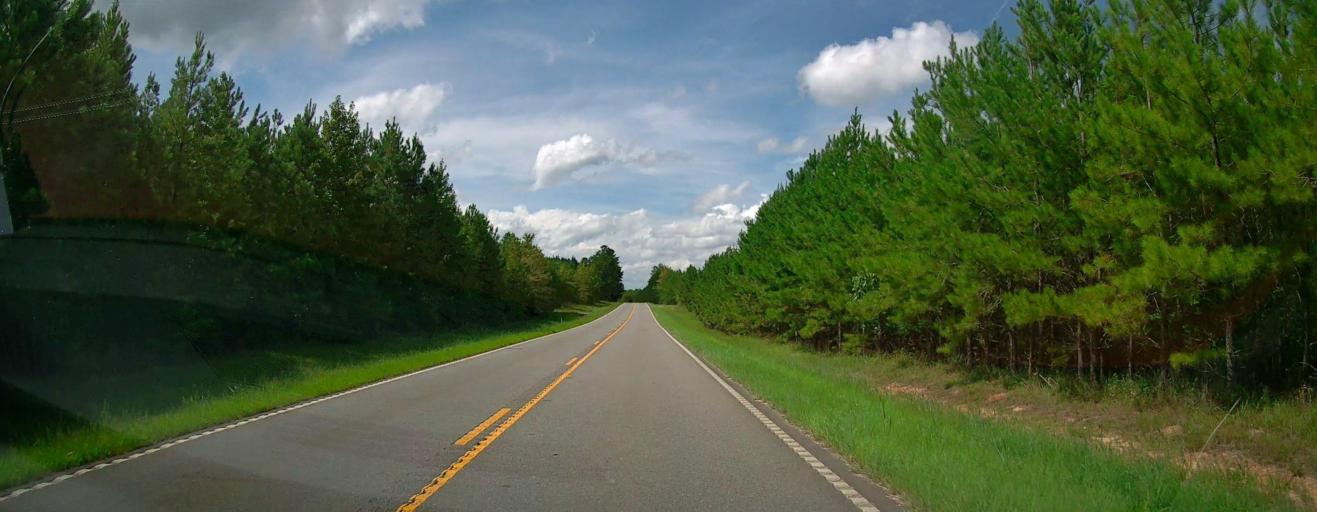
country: US
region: Georgia
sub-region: Talbot County
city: Talbotton
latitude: 32.6604
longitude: -84.5120
